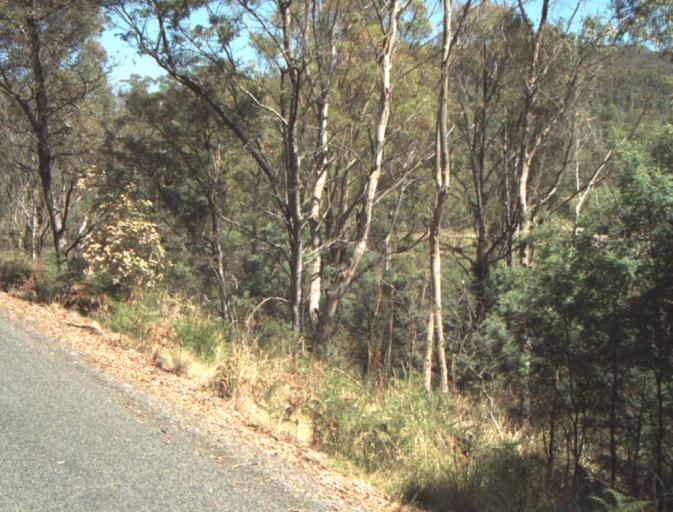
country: AU
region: Tasmania
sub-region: Launceston
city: Newstead
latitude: -41.3680
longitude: 147.3015
